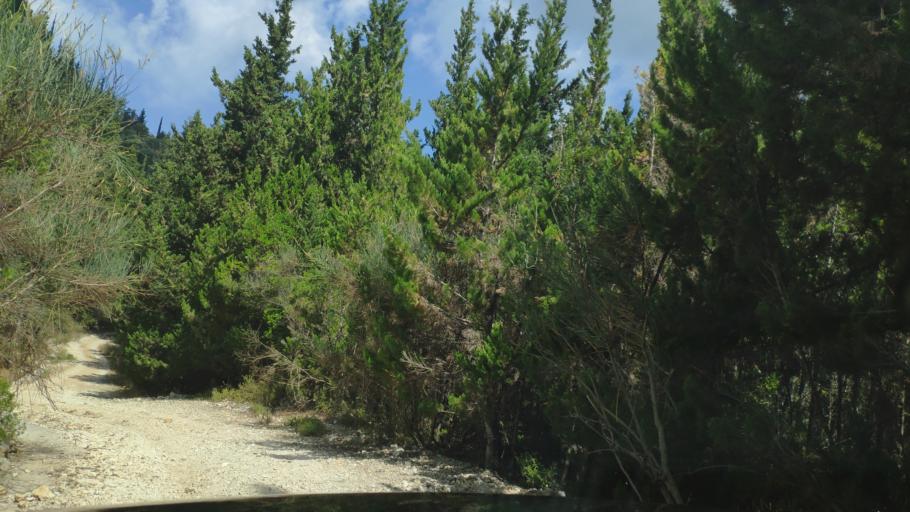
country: GR
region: Ionian Islands
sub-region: Lefkada
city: Lefkada
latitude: 38.7982
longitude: 20.6734
